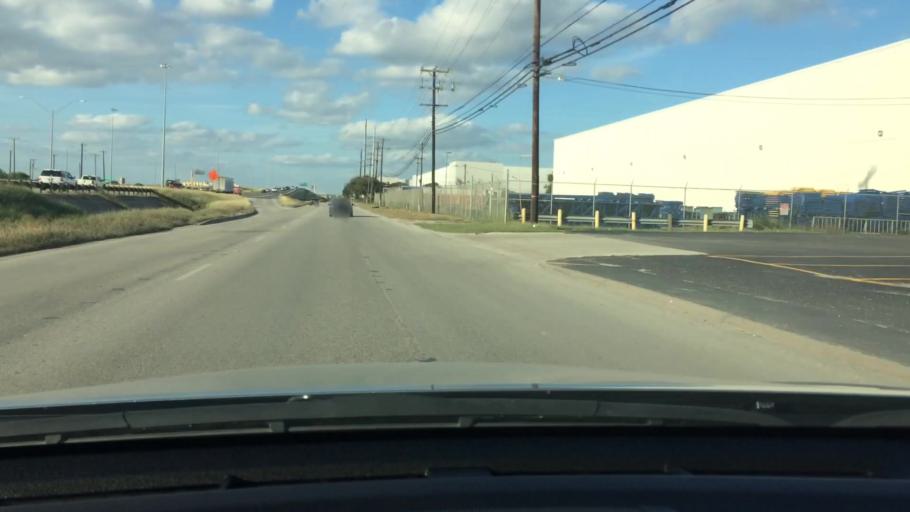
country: US
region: Texas
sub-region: Bexar County
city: Kirby
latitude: 29.4671
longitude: -98.4038
